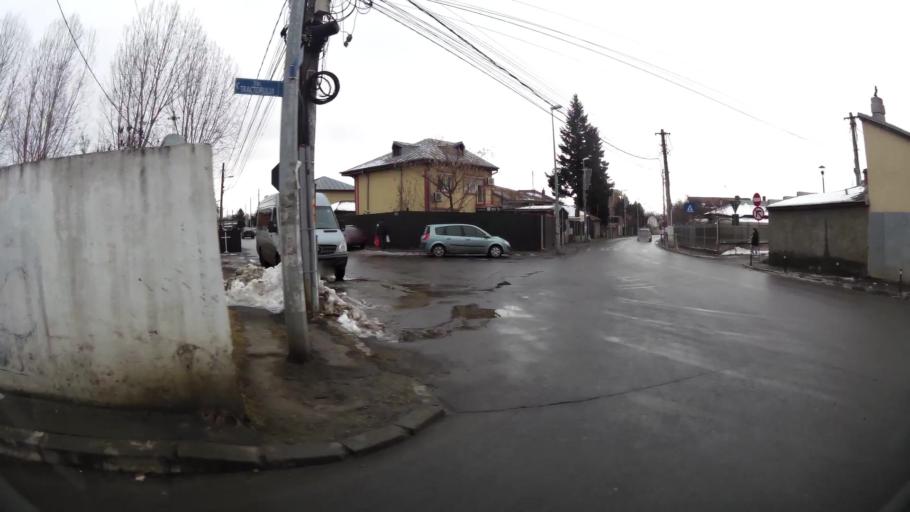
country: RO
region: Ilfov
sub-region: Comuna Pantelimon
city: Pantelimon
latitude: 44.4501
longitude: 26.2095
